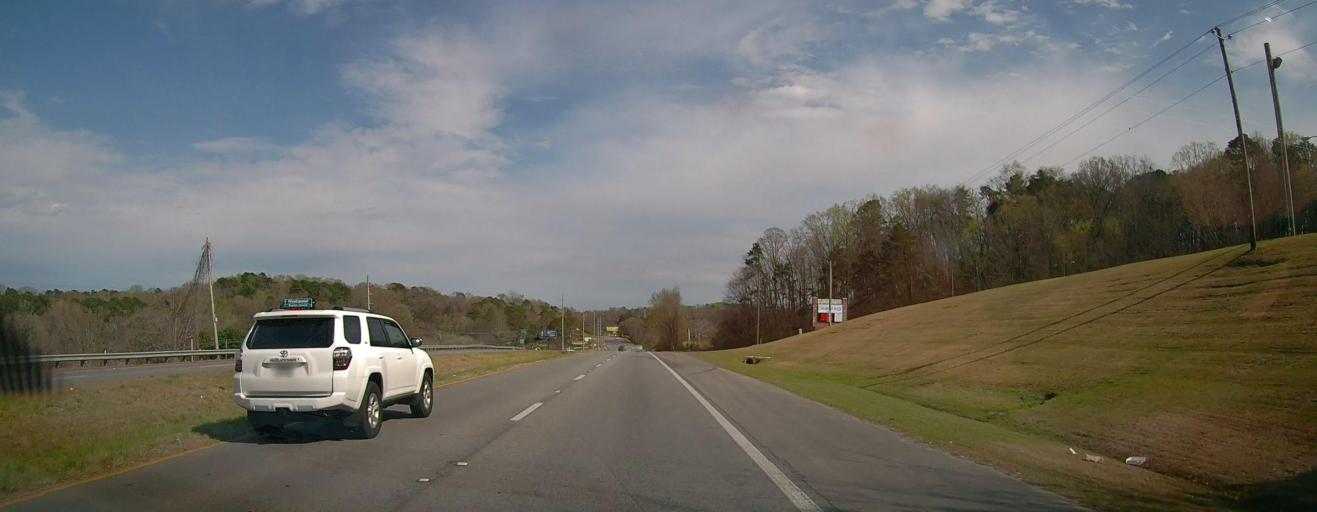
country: US
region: Alabama
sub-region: Jefferson County
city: Forestdale
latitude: 33.5791
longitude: -86.9171
